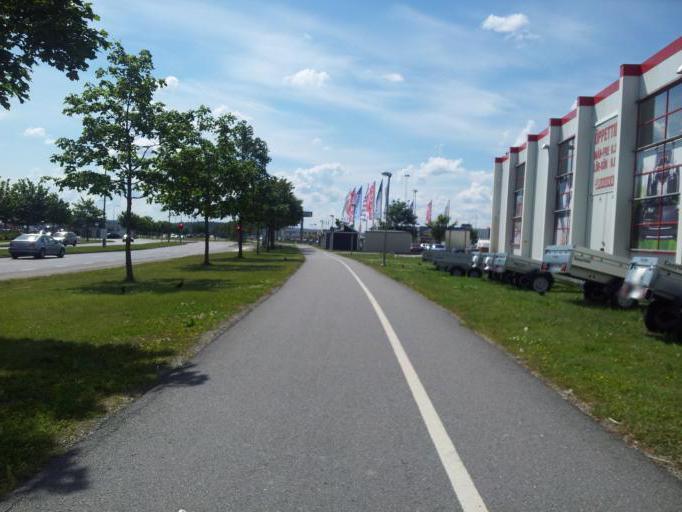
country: SE
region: Uppsala
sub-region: Uppsala Kommun
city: Saevja
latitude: 59.8486
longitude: 17.6904
